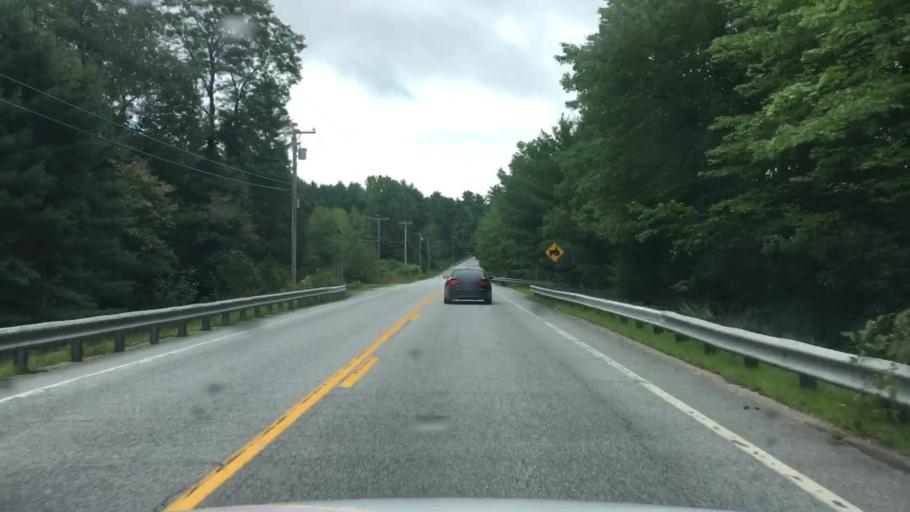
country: US
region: Maine
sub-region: Oxford County
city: Hiram
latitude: 43.8435
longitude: -70.7835
